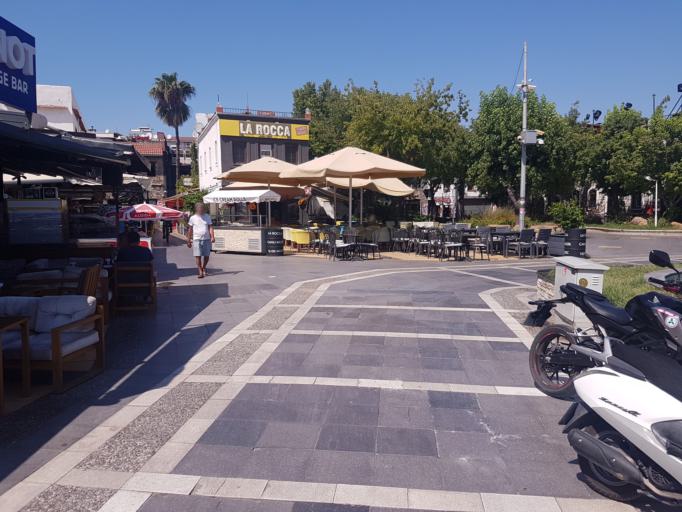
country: TR
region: Mugla
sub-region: Marmaris
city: Marmaris
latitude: 36.8521
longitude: 28.2755
